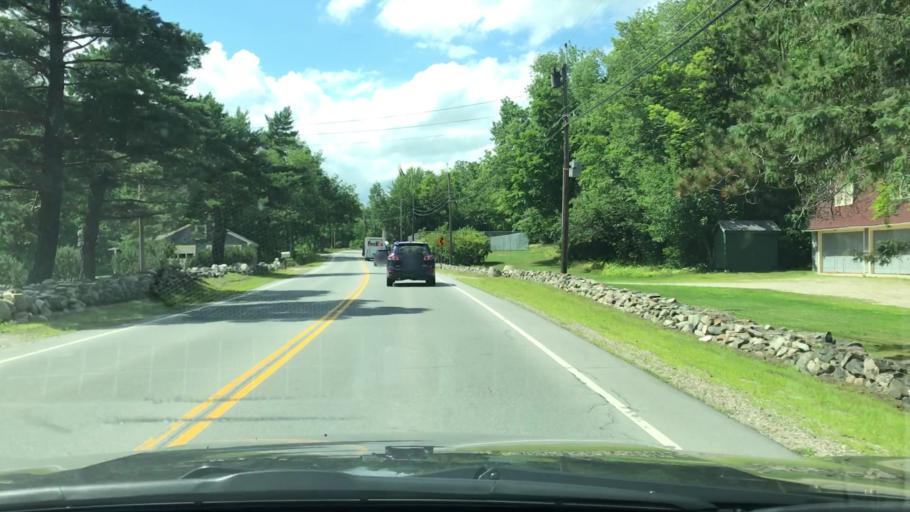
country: US
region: New Hampshire
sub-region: Coos County
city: Jefferson
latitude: 44.3701
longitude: -71.4044
